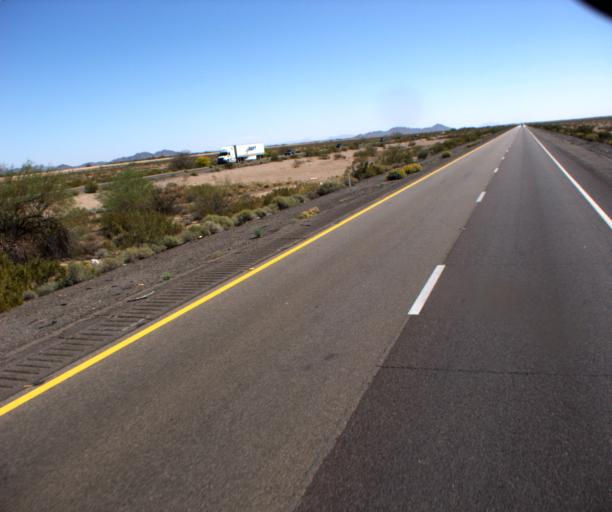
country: US
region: Arizona
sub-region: La Paz County
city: Salome
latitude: 33.6050
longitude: -113.5946
